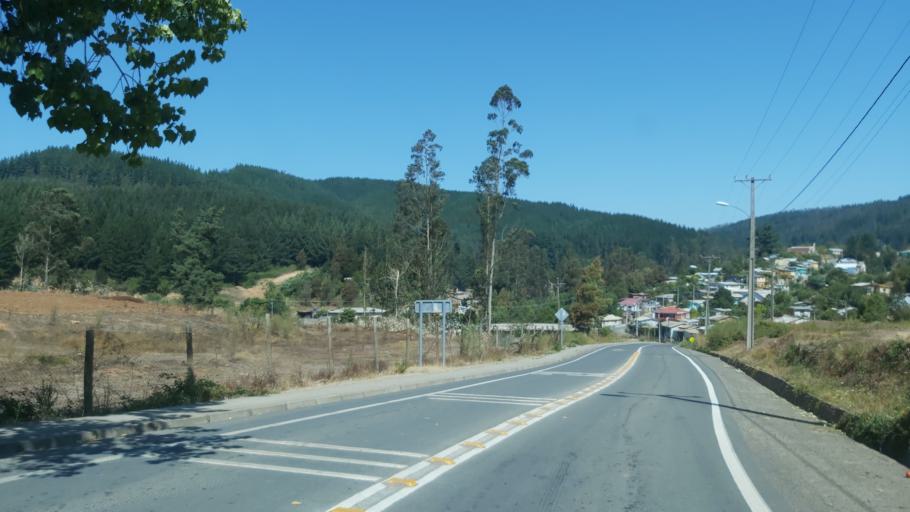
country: CL
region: Biobio
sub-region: Provincia de Concepcion
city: Tome
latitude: -36.5537
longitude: -72.8671
